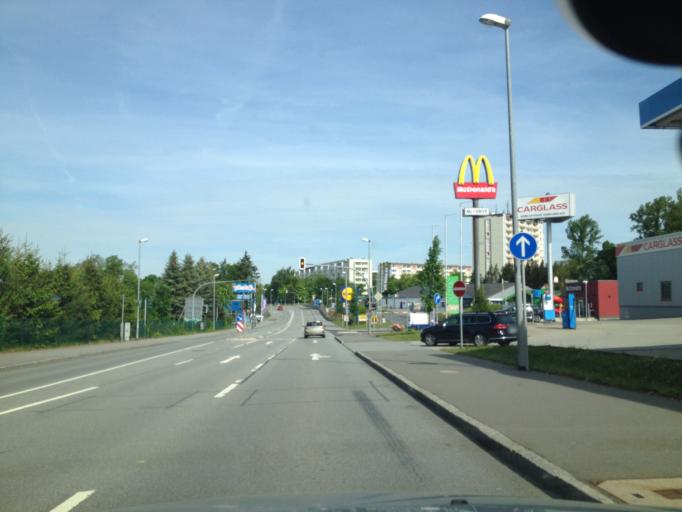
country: DE
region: Saxony
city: Annaberg-Buchholz
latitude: 50.5909
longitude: 13.0110
